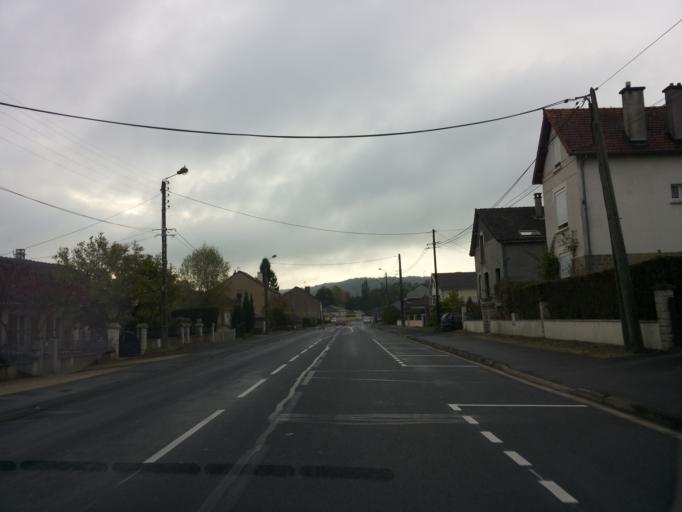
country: FR
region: Champagne-Ardenne
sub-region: Departement des Ardennes
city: Flize
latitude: 49.7044
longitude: 4.7723
